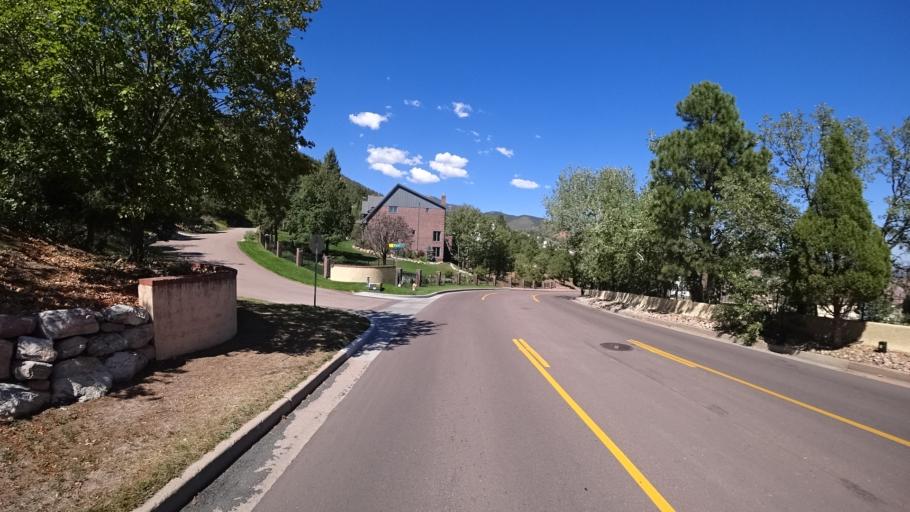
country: US
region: Colorado
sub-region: El Paso County
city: Colorado Springs
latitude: 38.7762
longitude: -104.8557
